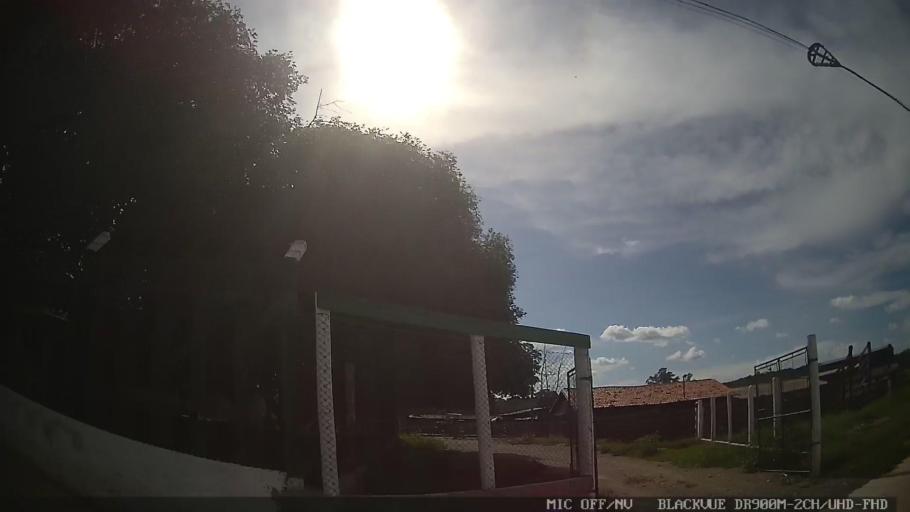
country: BR
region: Sao Paulo
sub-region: Conchas
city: Conchas
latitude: -23.0670
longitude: -47.9769
